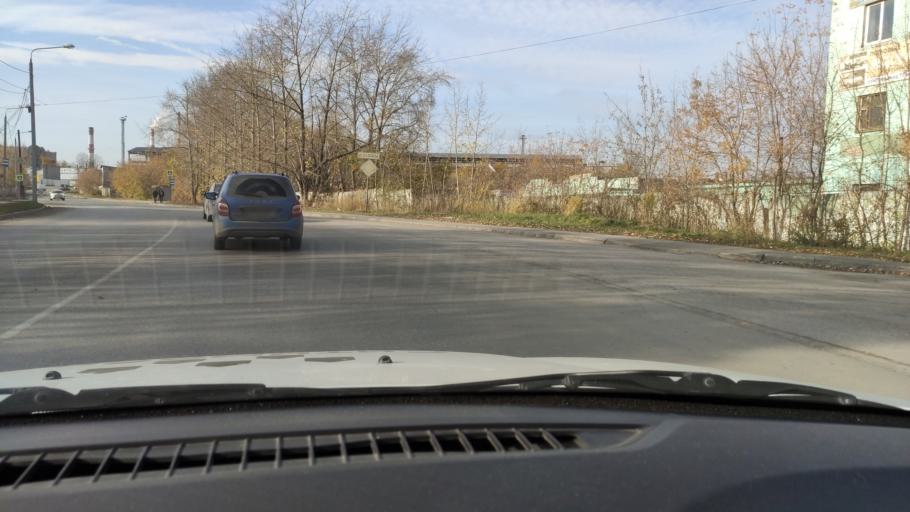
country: RU
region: Perm
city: Perm
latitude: 57.9837
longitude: 56.2752
